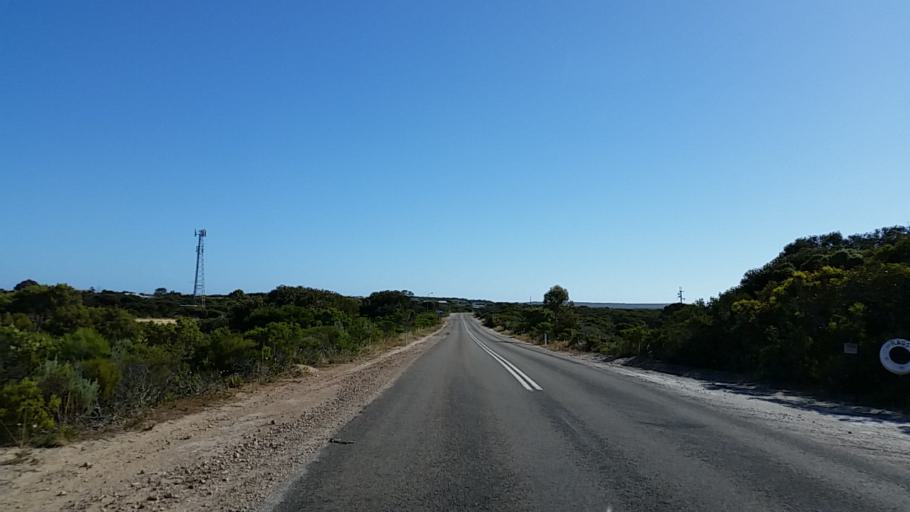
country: AU
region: South Australia
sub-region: Yorke Peninsula
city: Honiton
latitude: -35.2418
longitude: 136.9756
